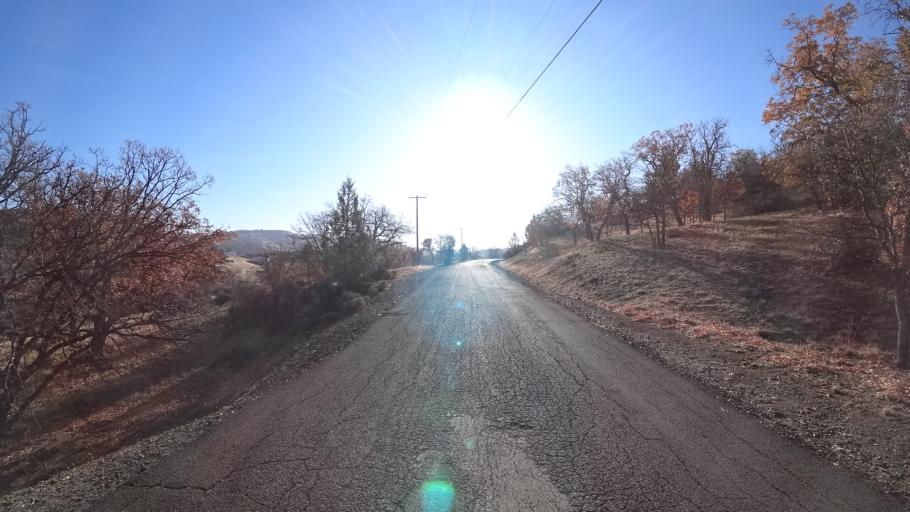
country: US
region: California
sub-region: Siskiyou County
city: Montague
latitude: 41.8926
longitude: -122.4951
